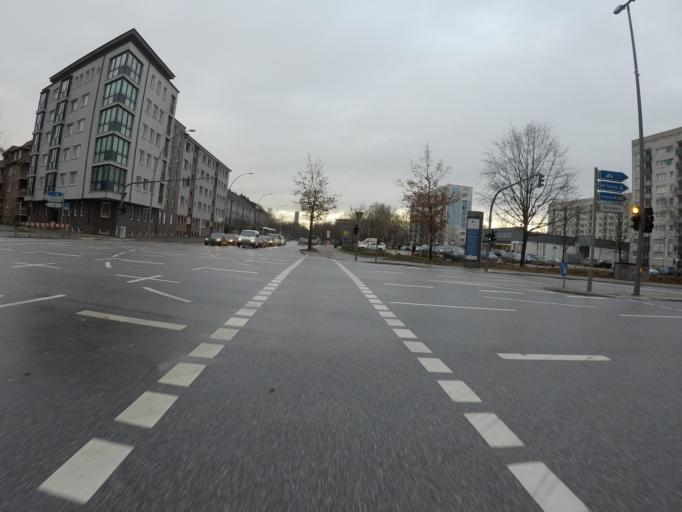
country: DE
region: Hamburg
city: Kleiner Grasbrook
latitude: 53.5005
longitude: 9.9915
